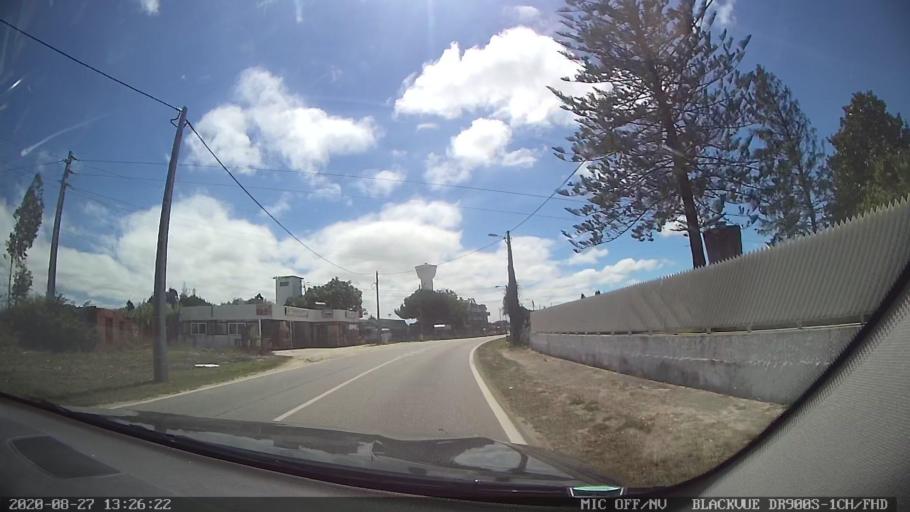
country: PT
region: Aveiro
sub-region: Vagos
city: Vagos
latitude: 40.5382
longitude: -8.6766
